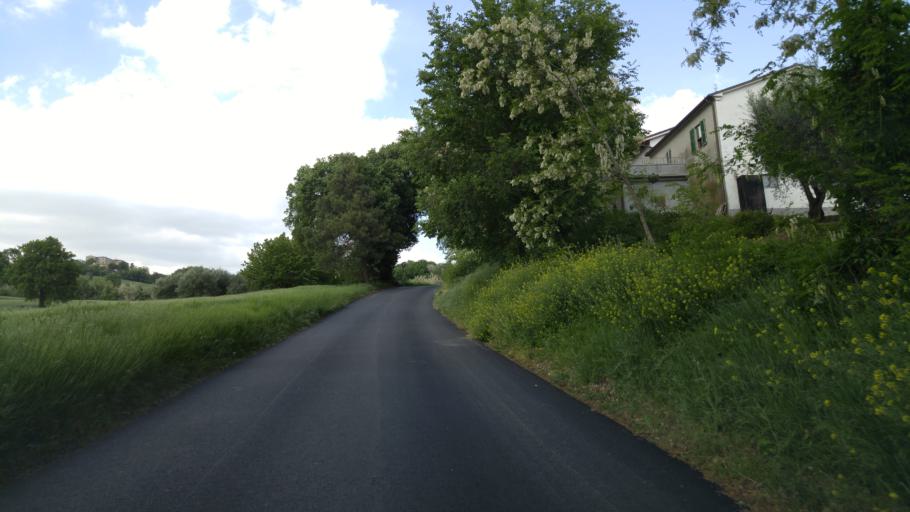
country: IT
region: The Marches
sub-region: Provincia di Pesaro e Urbino
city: Montefelcino
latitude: 43.7280
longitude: 12.8323
